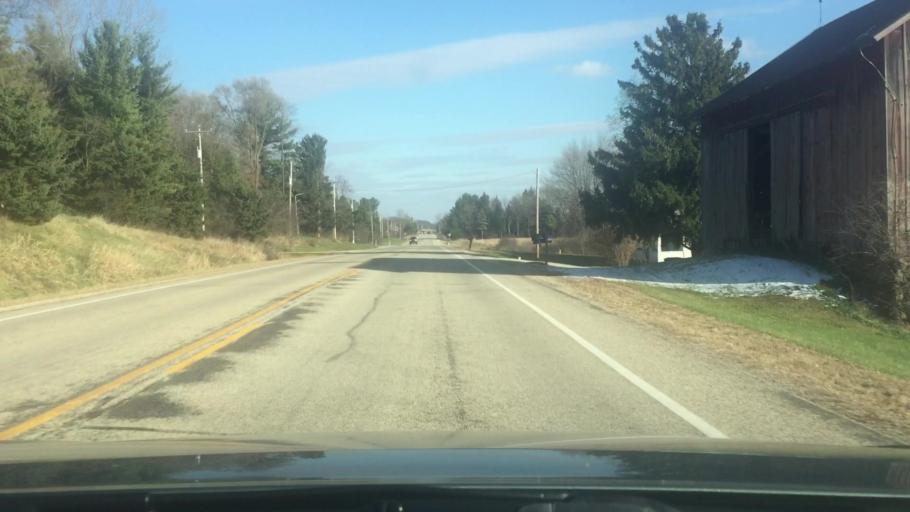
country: US
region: Wisconsin
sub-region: Jefferson County
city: Fort Atkinson
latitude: 42.9390
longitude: -88.7680
